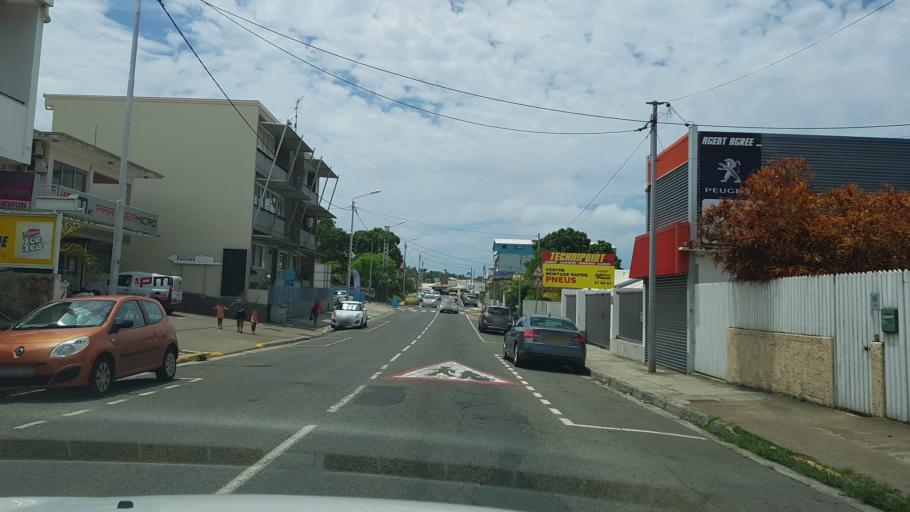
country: NC
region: South Province
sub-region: Noumea
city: Noumea
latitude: -22.2832
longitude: 166.4533
